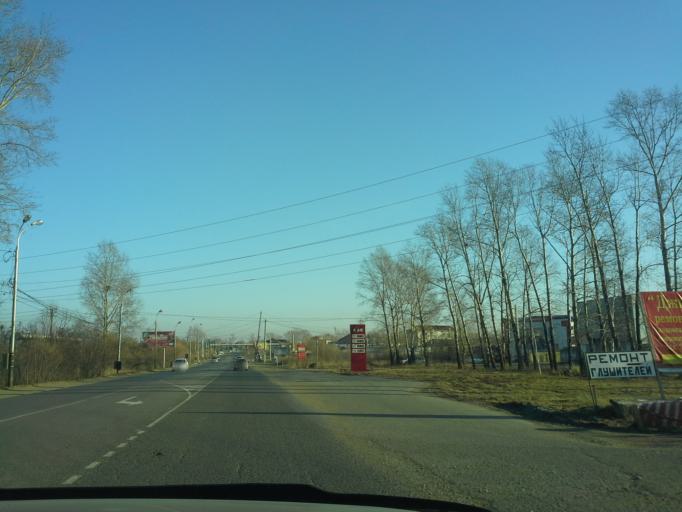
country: RU
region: Khabarovsk Krai
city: Topolevo
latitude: 48.4752
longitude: 135.1685
